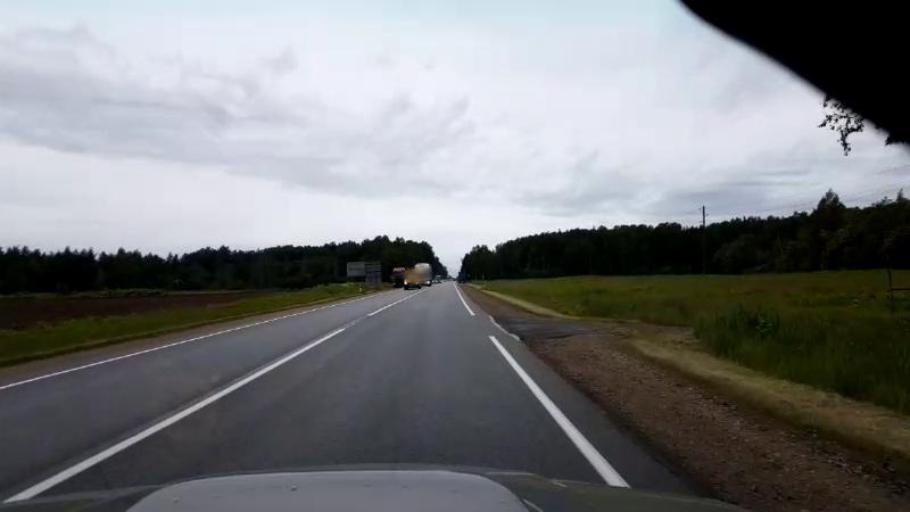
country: LV
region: Kekava
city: Kekava
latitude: 56.8134
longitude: 24.2664
